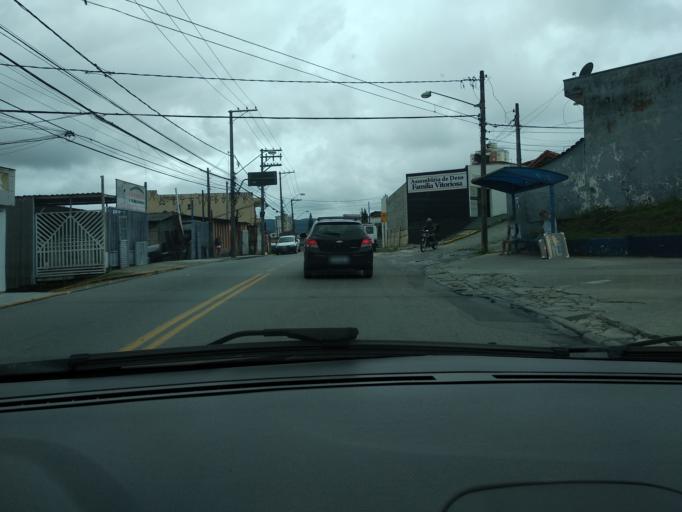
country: BR
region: Sao Paulo
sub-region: Mogi das Cruzes
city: Mogi das Cruzes
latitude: -23.5349
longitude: -46.1937
